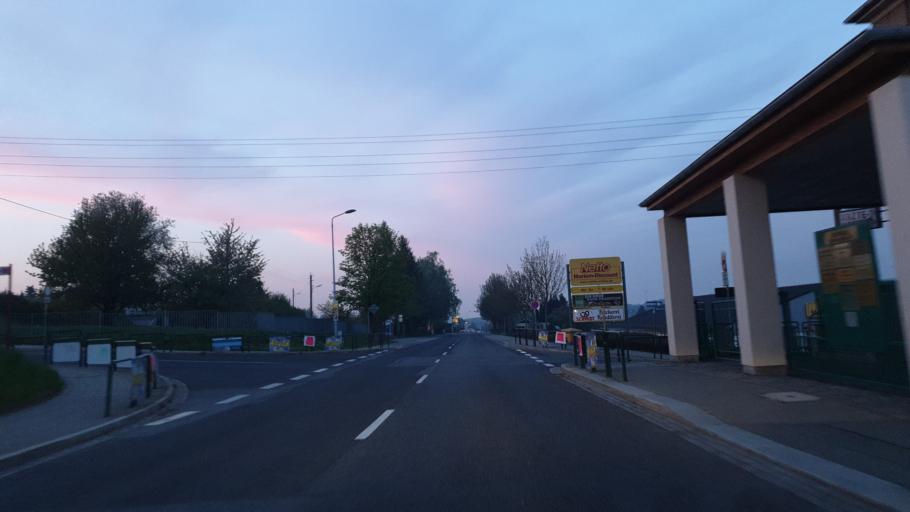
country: DE
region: Saxony
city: Stollberg
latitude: 50.7129
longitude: 12.7797
